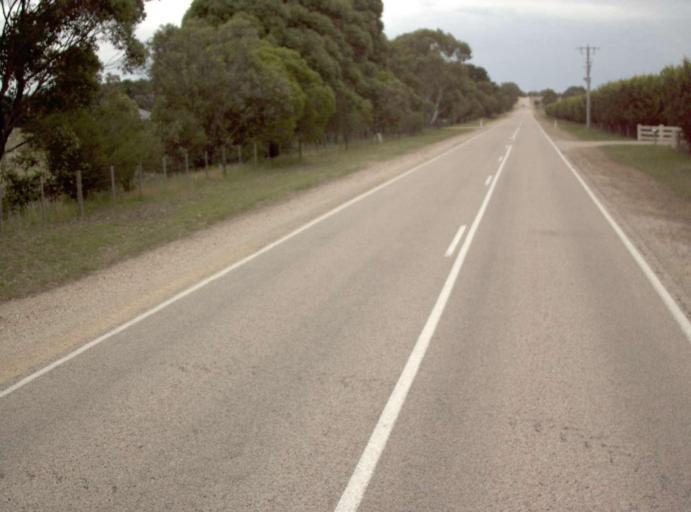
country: AU
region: Victoria
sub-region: East Gippsland
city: Bairnsdale
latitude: -37.8649
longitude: 147.5624
